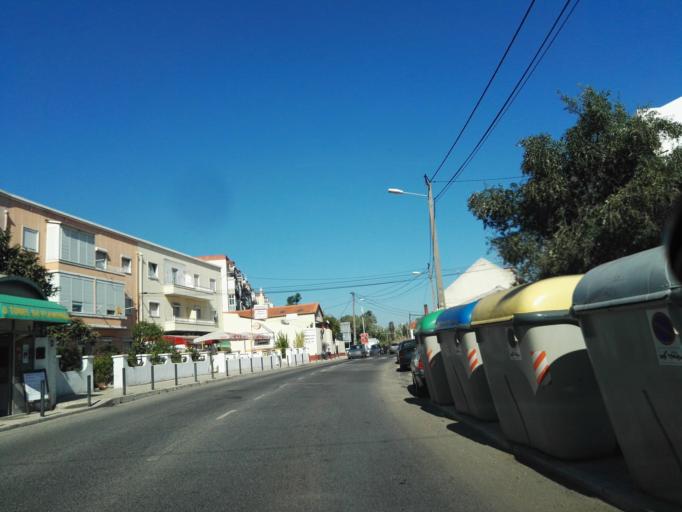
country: PT
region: Lisbon
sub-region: Odivelas
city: Povoa de Santo Adriao
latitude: 38.8089
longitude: -9.1572
